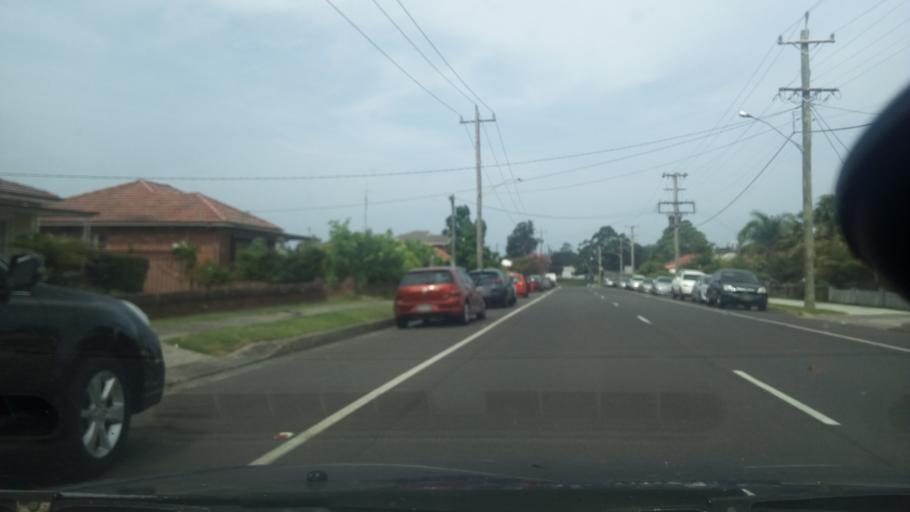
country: AU
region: New South Wales
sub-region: Wollongong
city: Gwynneville
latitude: -34.4125
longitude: 150.8883
